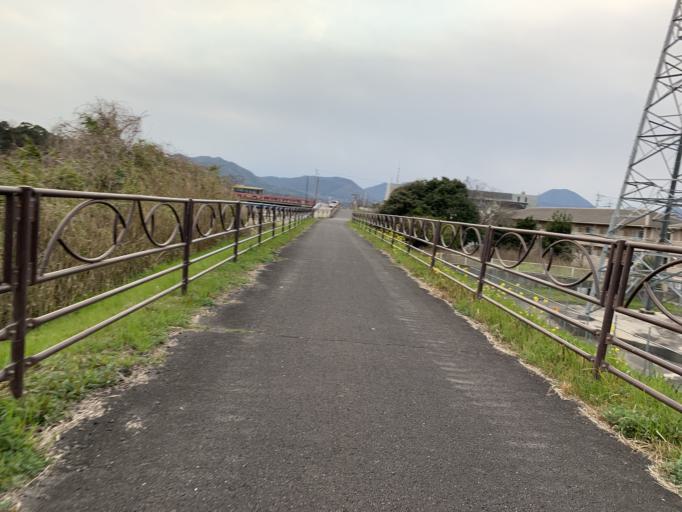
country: JP
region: Oita
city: Bungo-Takada-shi
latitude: 33.5350
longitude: 131.3519
